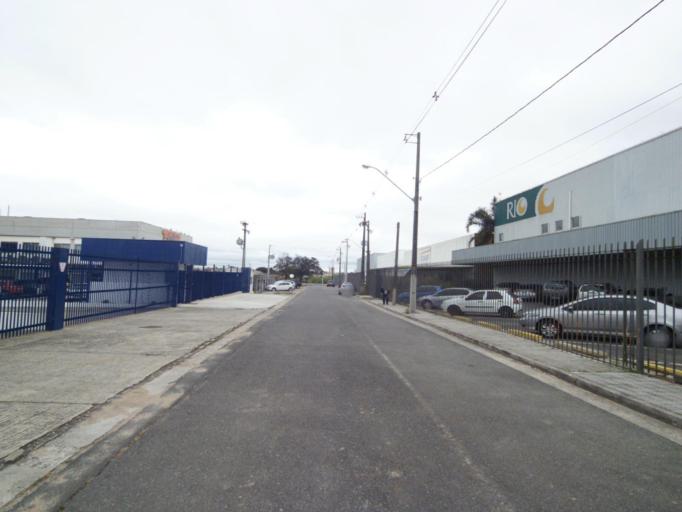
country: BR
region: Parana
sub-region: Sao Jose Dos Pinhais
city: Sao Jose dos Pinhais
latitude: -25.5310
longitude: -49.1789
